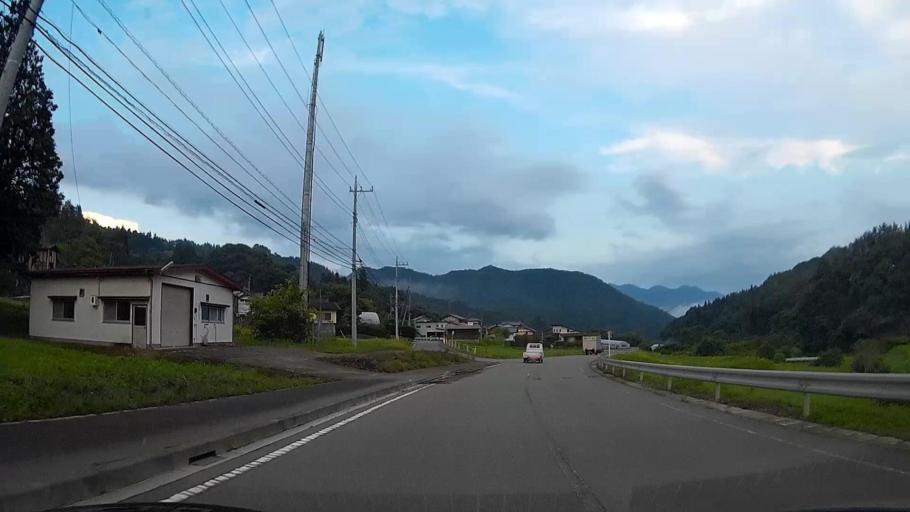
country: JP
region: Gunma
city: Nakanojomachi
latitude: 36.5262
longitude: 138.7479
